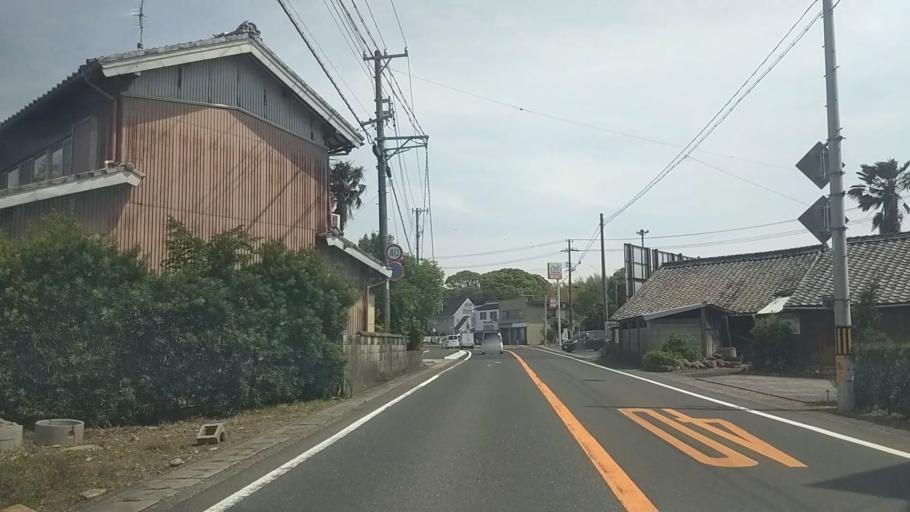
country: JP
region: Shizuoka
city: Kosai-shi
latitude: 34.7941
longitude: 137.5771
